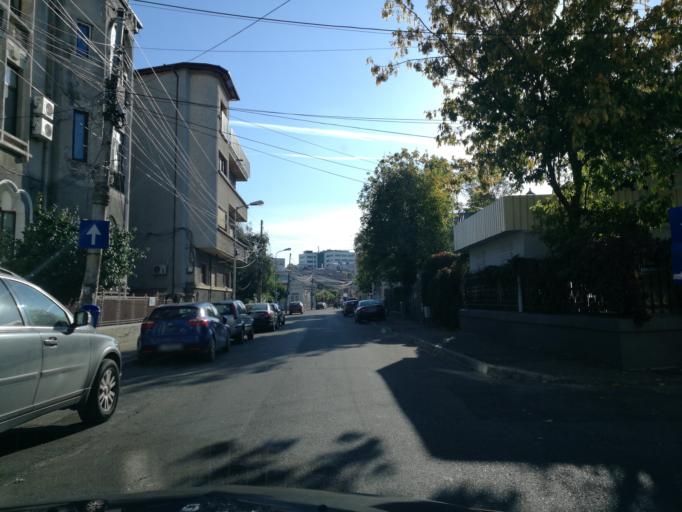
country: RO
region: Bucuresti
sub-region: Municipiul Bucuresti
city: Bucharest
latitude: 44.4449
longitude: 26.1089
